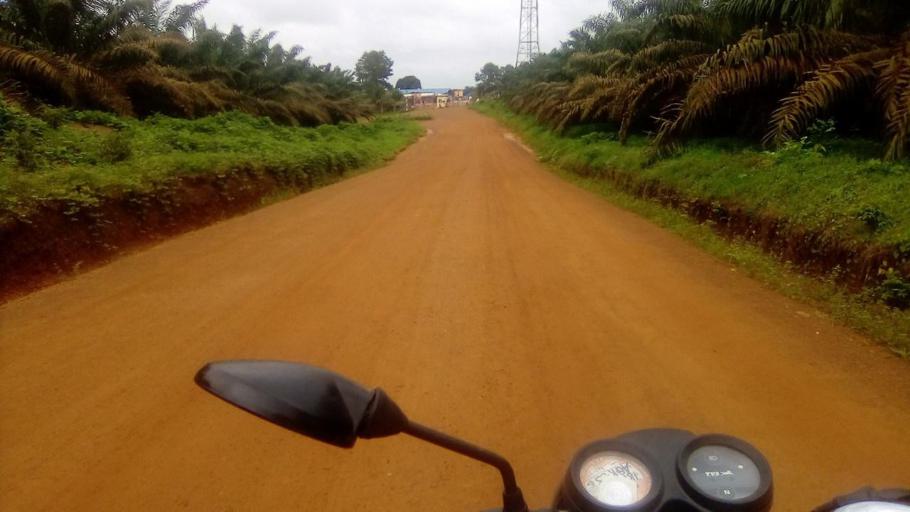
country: SL
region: Southern Province
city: Tongole
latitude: 7.4287
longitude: -11.8492
